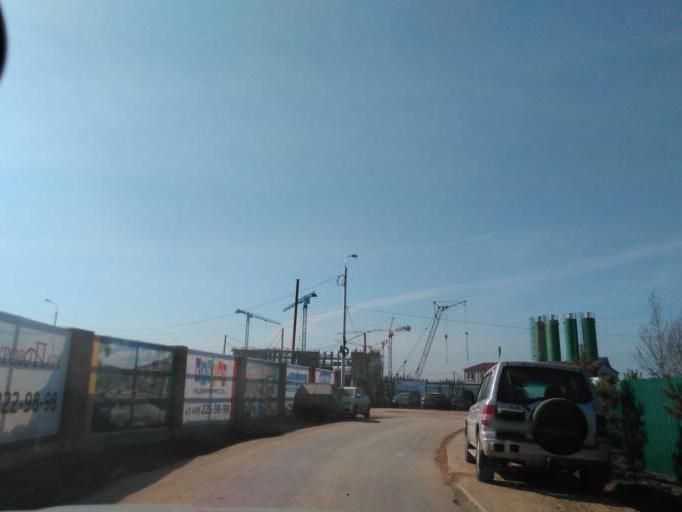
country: RU
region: Moskovskaya
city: Opalikha
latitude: 55.8760
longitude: 37.2583
